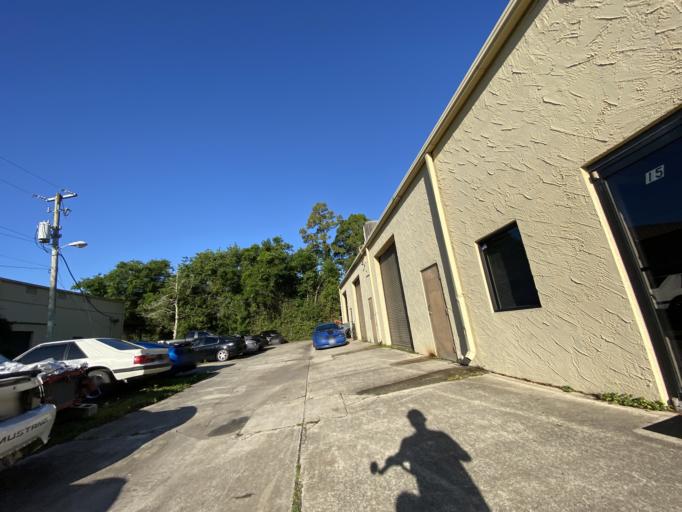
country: US
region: Florida
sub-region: Volusia County
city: Port Orange
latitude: 29.1471
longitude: -80.9942
